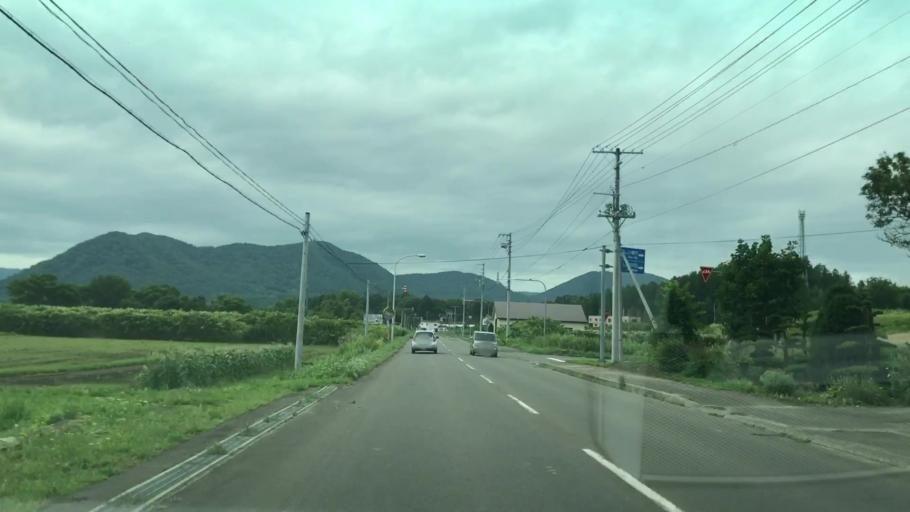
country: JP
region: Hokkaido
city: Yoichi
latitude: 43.0924
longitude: 140.8184
